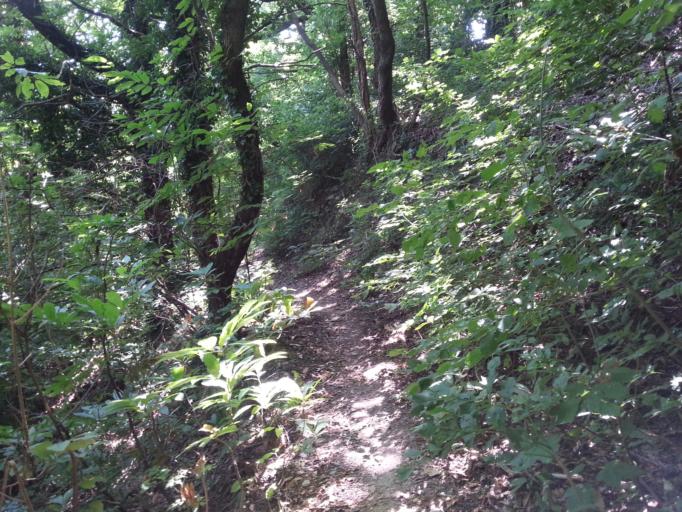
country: IT
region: Lombardy
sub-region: Provincia di Lecco
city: Ballabio
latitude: 45.8722
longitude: 9.4159
